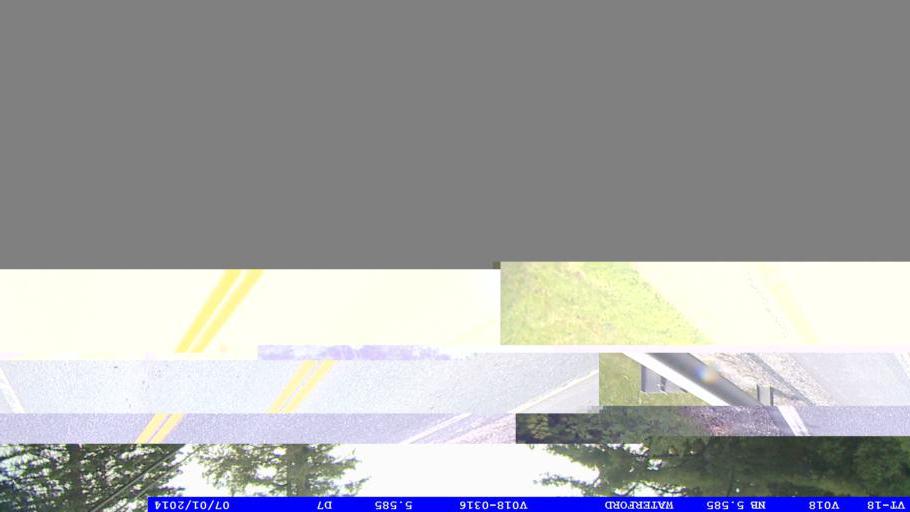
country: US
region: Vermont
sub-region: Caledonia County
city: Saint Johnsbury
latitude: 44.4103
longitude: -71.9310
